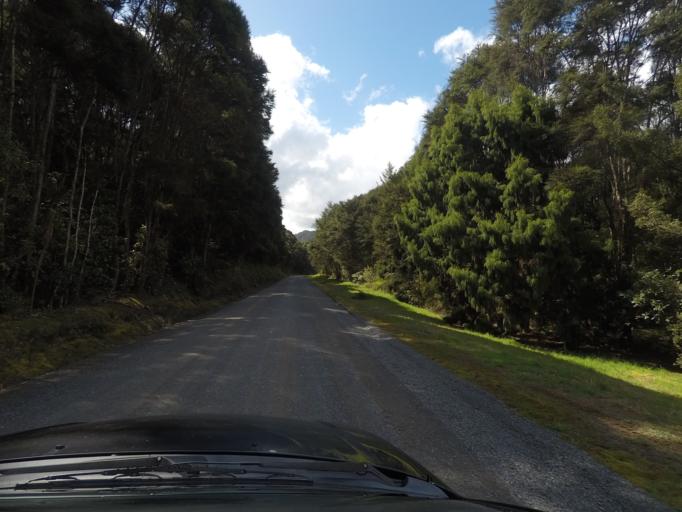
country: NZ
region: Auckland
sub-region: Auckland
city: Red Hill
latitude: -37.0955
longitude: 175.1511
